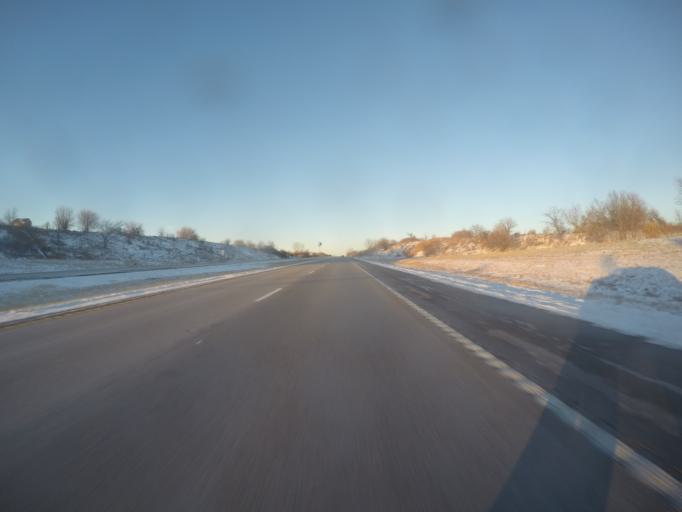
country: US
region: Missouri
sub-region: Platte County
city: Platte City
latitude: 39.3113
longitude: -94.7579
